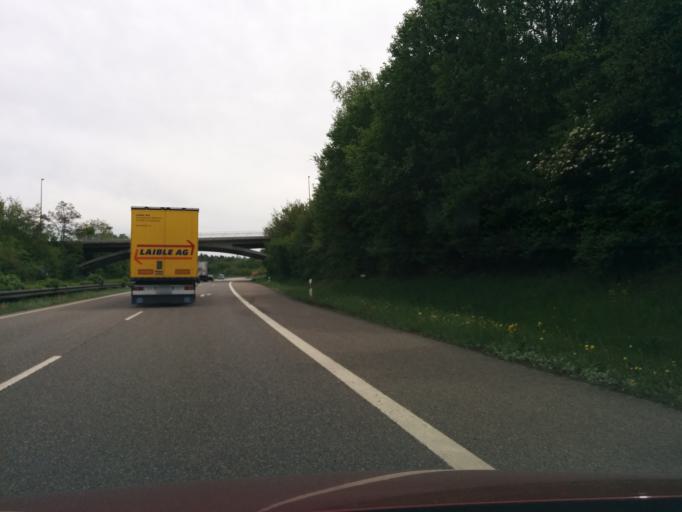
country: DE
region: Baden-Wuerttemberg
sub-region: Regierungsbezirk Stuttgart
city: Boeblingen
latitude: 48.6763
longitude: 8.9769
